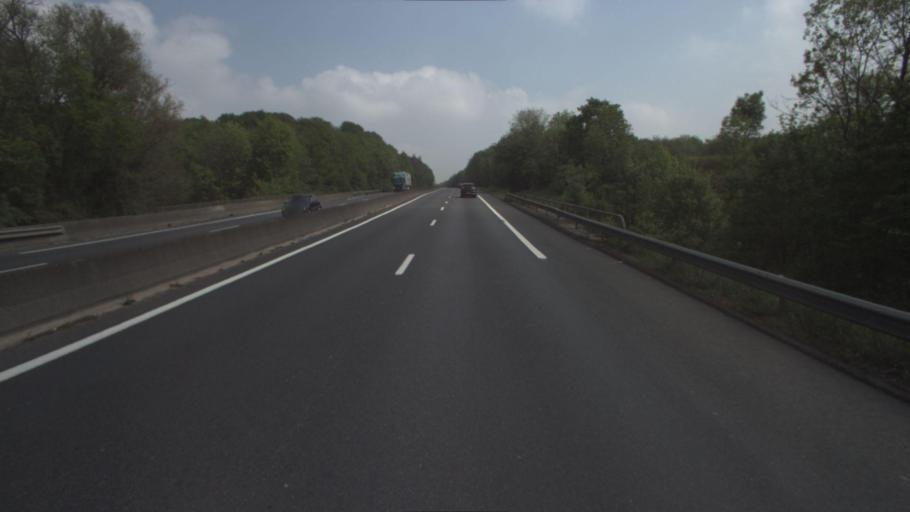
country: FR
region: Ile-de-France
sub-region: Departement de Seine-et-Marne
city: Saint-Mard
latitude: 49.0436
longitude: 2.6885
